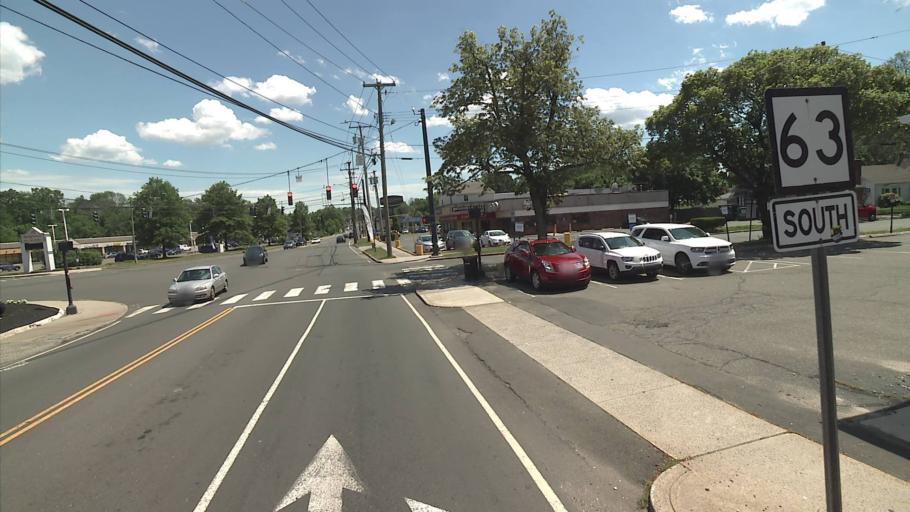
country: US
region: Connecticut
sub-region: New Haven County
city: Woodbridge
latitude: 41.3351
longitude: -72.9773
